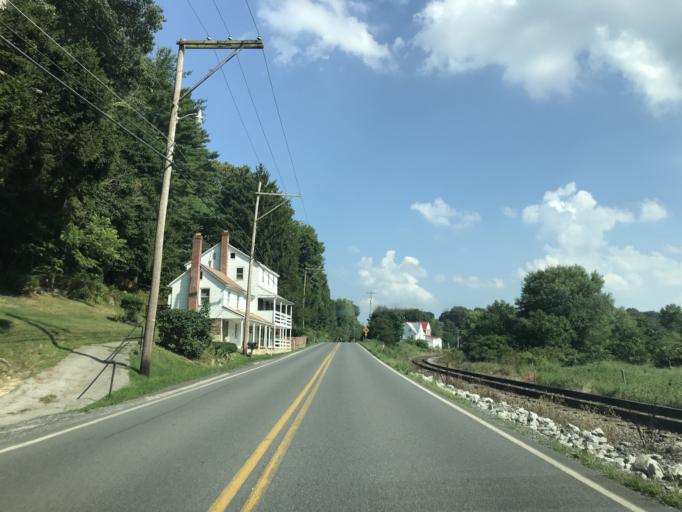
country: US
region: Pennsylvania
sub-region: York County
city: Glen Rock
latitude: 39.7607
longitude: -76.8178
